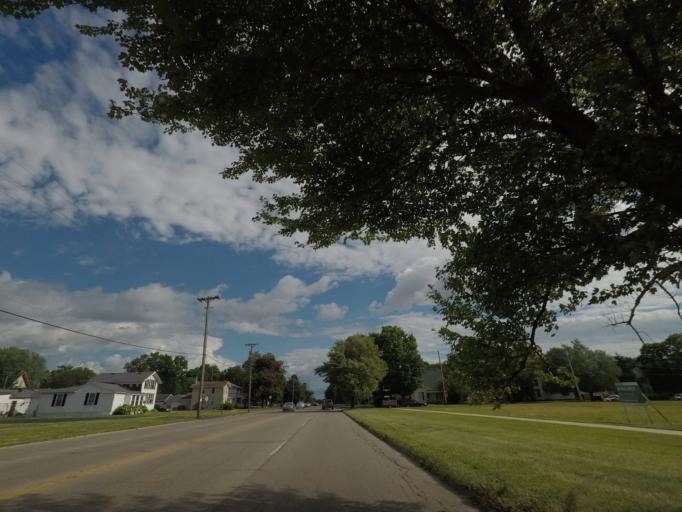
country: US
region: Wisconsin
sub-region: Rock County
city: Janesville
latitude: 42.6774
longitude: -89.0320
